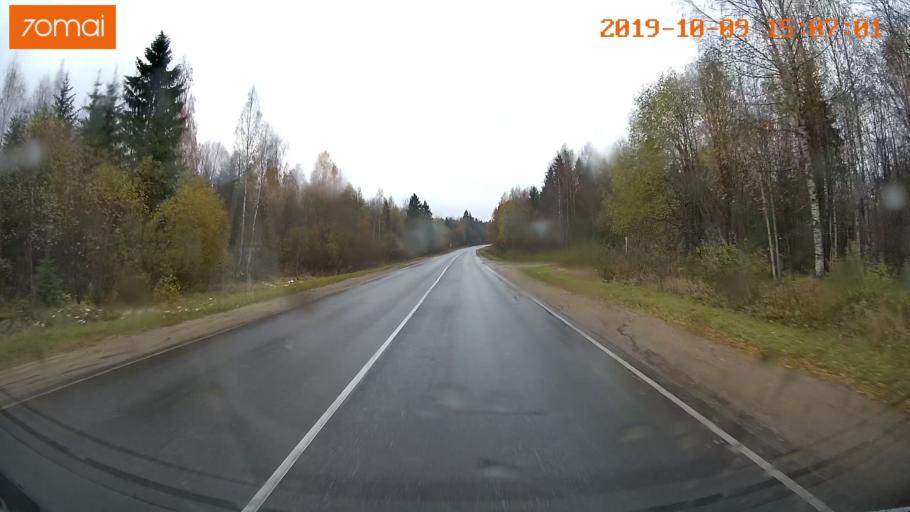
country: RU
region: Kostroma
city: Susanino
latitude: 58.2247
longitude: 41.6538
